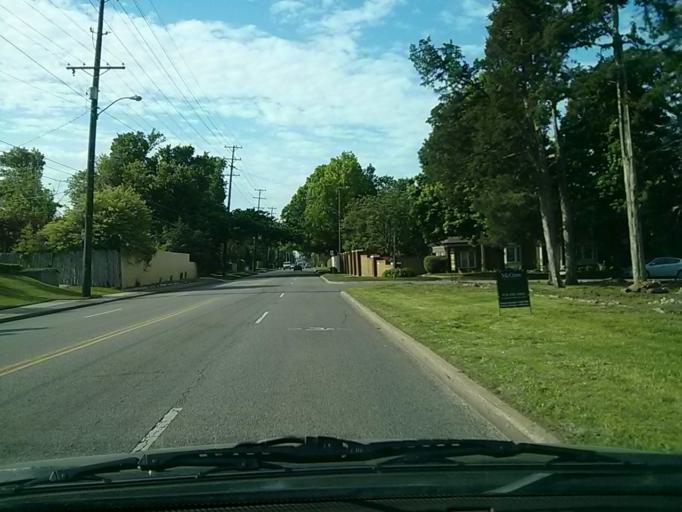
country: US
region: Oklahoma
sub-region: Tulsa County
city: Tulsa
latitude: 36.1241
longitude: -95.9758
